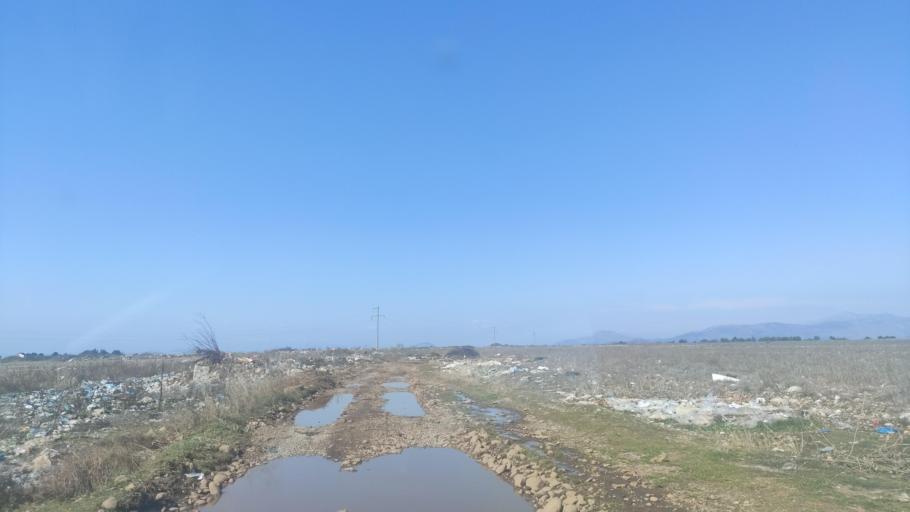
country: AL
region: Shkoder
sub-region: Rrethi i Malesia e Madhe
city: Koplik
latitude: 42.2281
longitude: 19.4372
